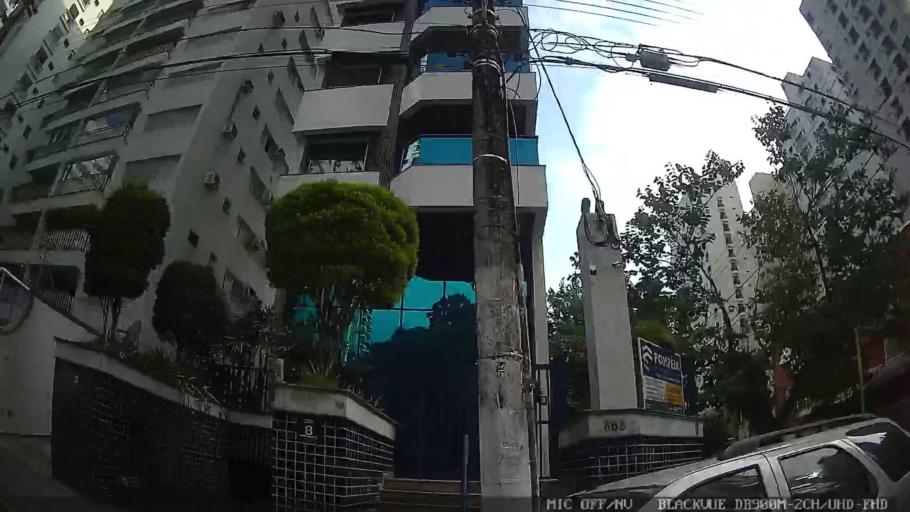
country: BR
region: Sao Paulo
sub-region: Guaruja
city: Guaruja
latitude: -23.9970
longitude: -46.2637
